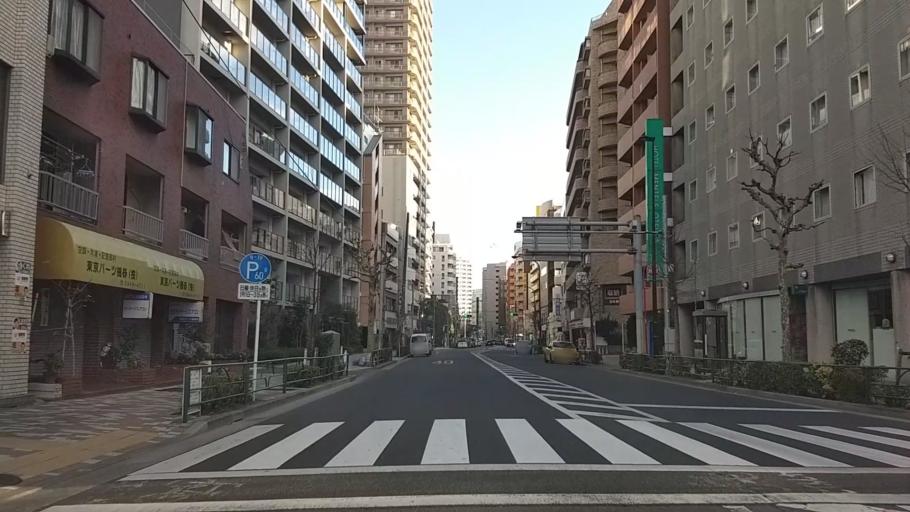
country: JP
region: Tokyo
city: Tokyo
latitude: 35.7351
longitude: 139.7270
